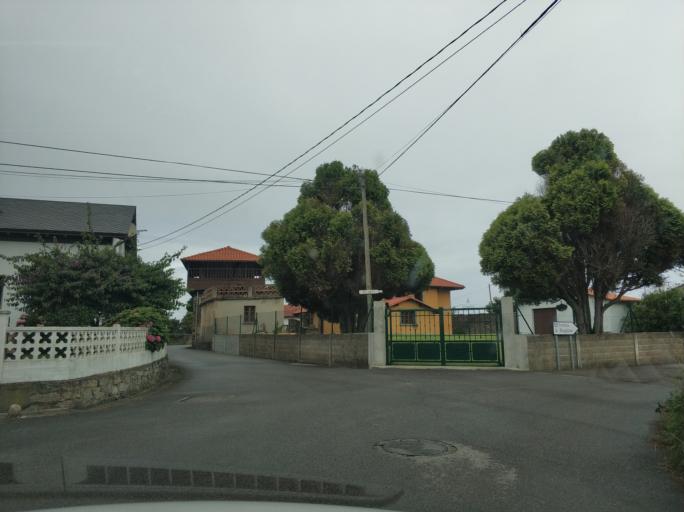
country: ES
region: Asturias
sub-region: Province of Asturias
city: Salas
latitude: 43.5507
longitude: -6.3821
